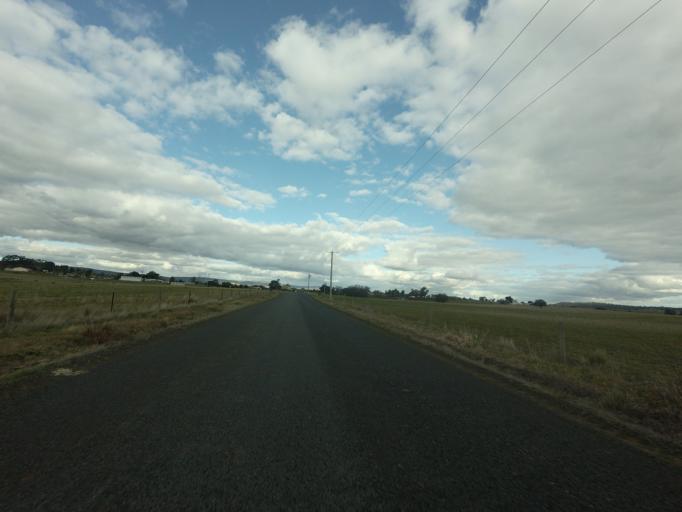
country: AU
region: Tasmania
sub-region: Northern Midlands
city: Evandale
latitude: -41.9197
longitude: 147.4792
